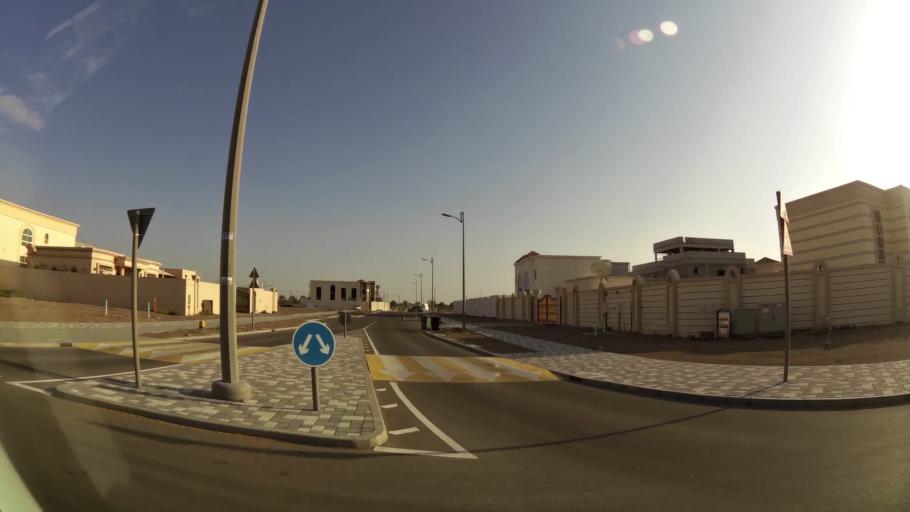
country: AE
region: Abu Dhabi
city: Al Ain
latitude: 24.0940
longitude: 55.8549
